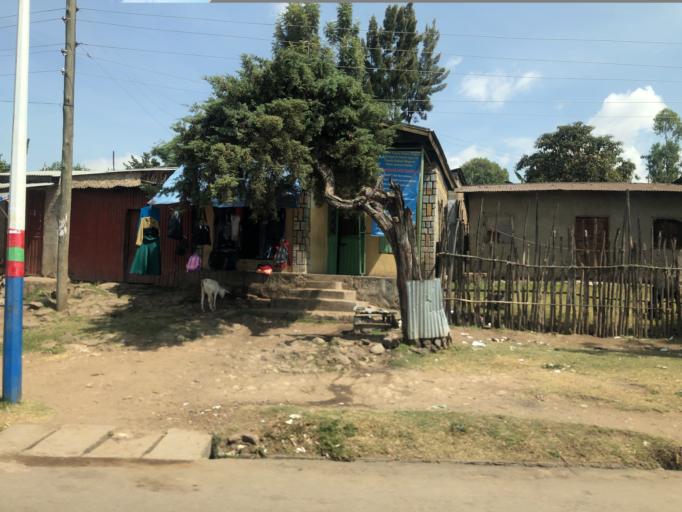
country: ET
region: Oromiya
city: Shashemene
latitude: 7.2681
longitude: 38.6565
